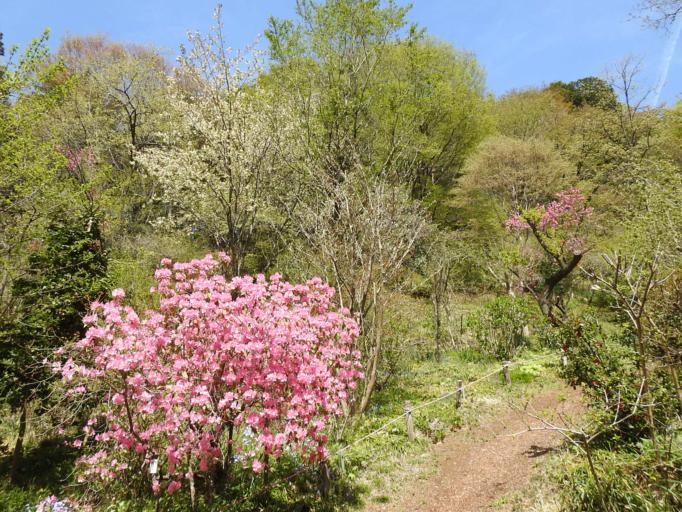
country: JP
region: Tochigi
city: Tochigi
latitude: 36.4496
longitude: 139.6979
